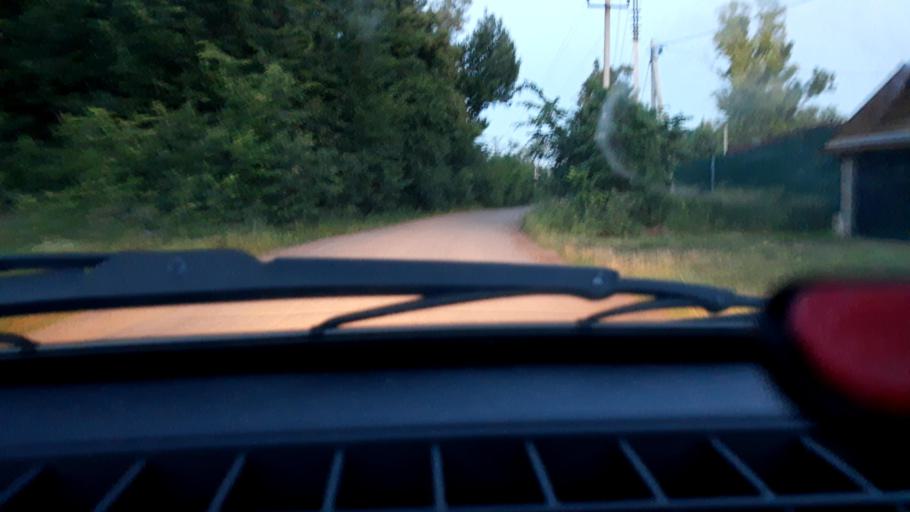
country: RU
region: Bashkortostan
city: Avdon
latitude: 54.4646
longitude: 55.8347
